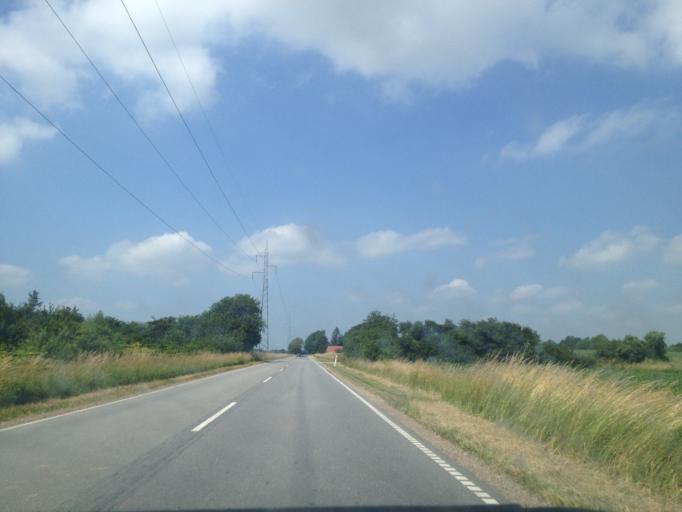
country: DK
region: South Denmark
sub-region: Kolding Kommune
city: Vamdrup
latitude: 55.3616
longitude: 9.2850
